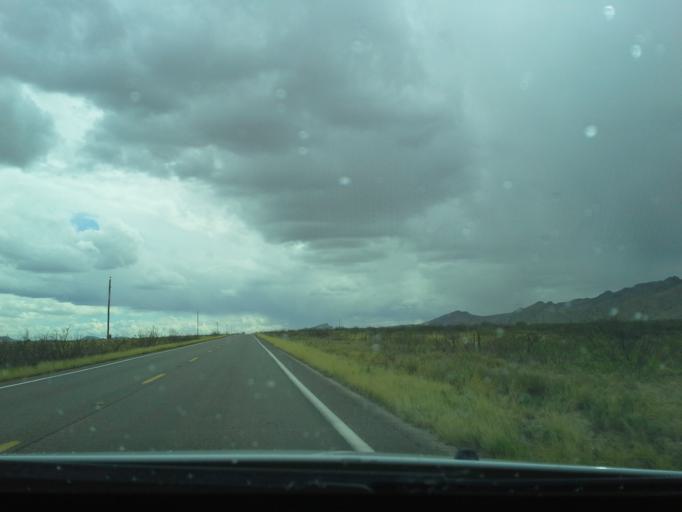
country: US
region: Arizona
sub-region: Cochise County
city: Douglas
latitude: 31.7855
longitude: -109.0669
